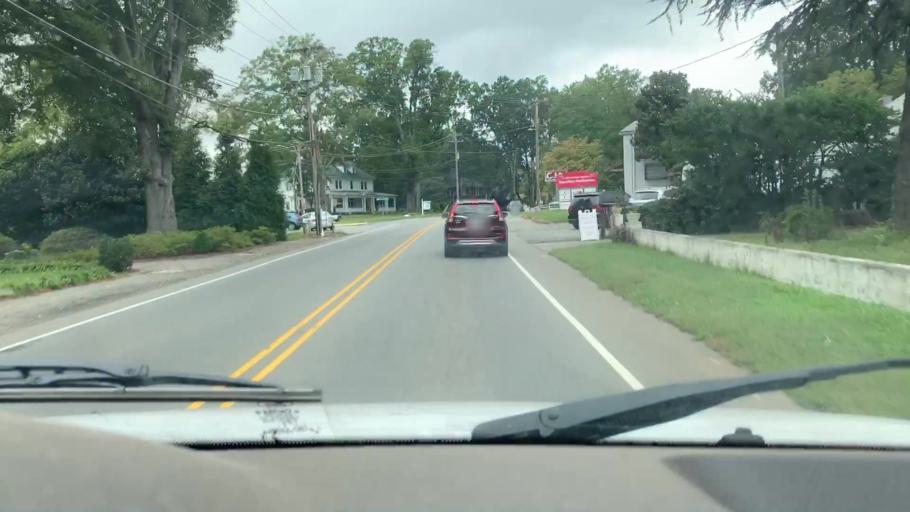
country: US
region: North Carolina
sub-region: Mecklenburg County
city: Huntersville
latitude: 35.4043
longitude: -80.8407
